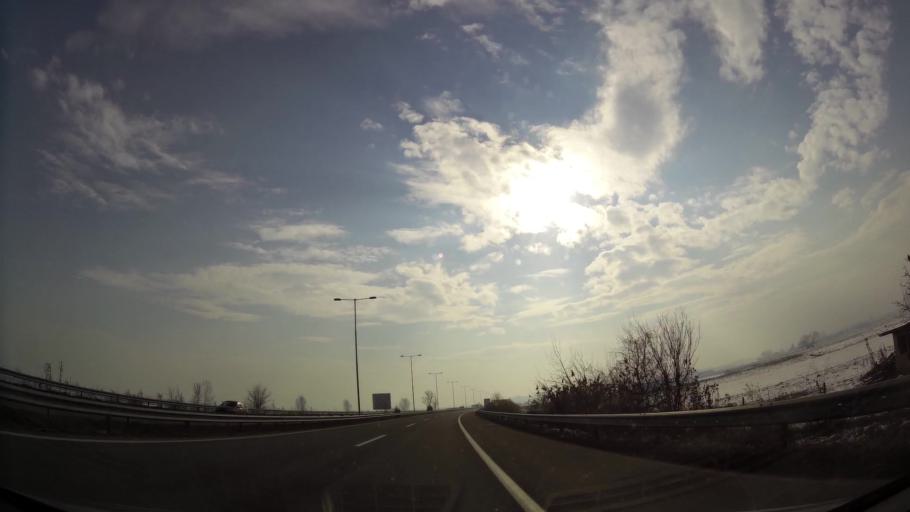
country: MK
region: Aracinovo
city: Arachinovo
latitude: 42.0062
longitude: 21.5349
